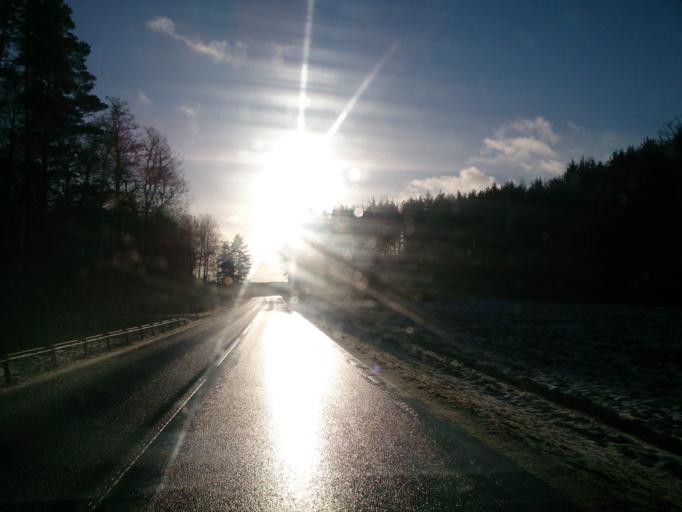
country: SE
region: OEstergoetland
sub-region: Atvidabergs Kommun
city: Atvidaberg
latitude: 58.3018
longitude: 15.8879
